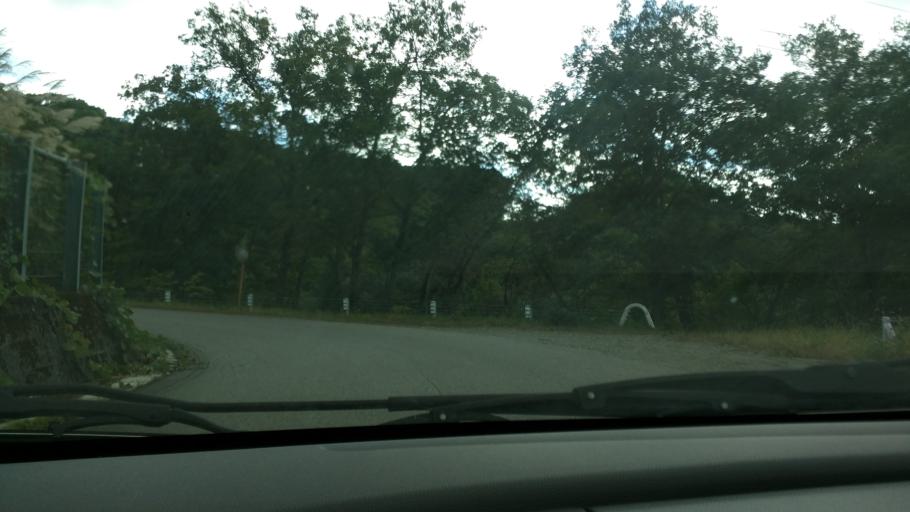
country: JP
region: Fukushima
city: Kitakata
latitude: 37.4583
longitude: 139.7117
